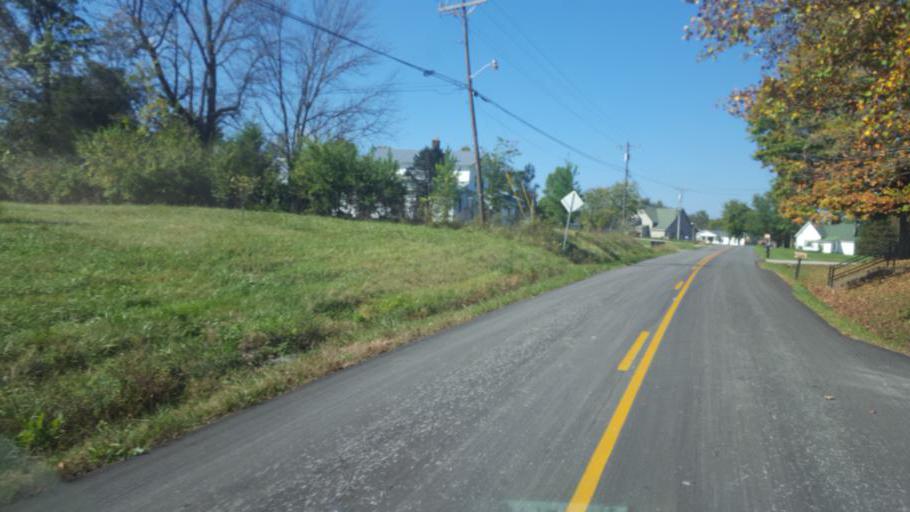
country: US
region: Kentucky
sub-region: Fleming County
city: Flemingsburg
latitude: 38.4735
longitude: -83.5916
